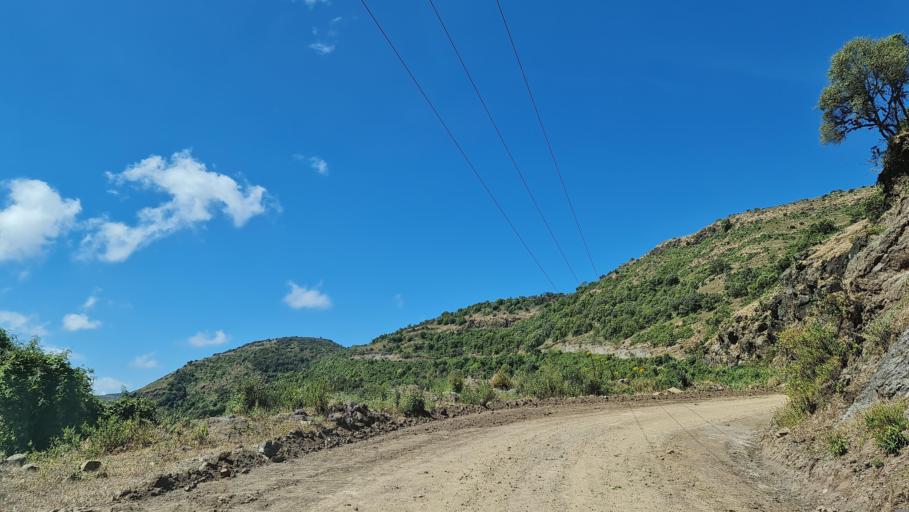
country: ET
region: Amhara
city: Debark'
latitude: 13.2355
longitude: 38.0604
